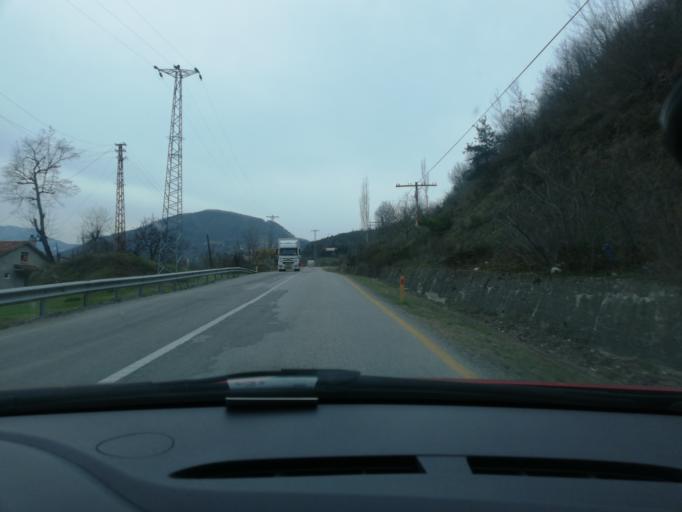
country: TR
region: Kastamonu
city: Inebolu
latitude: 41.9395
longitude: 33.7592
